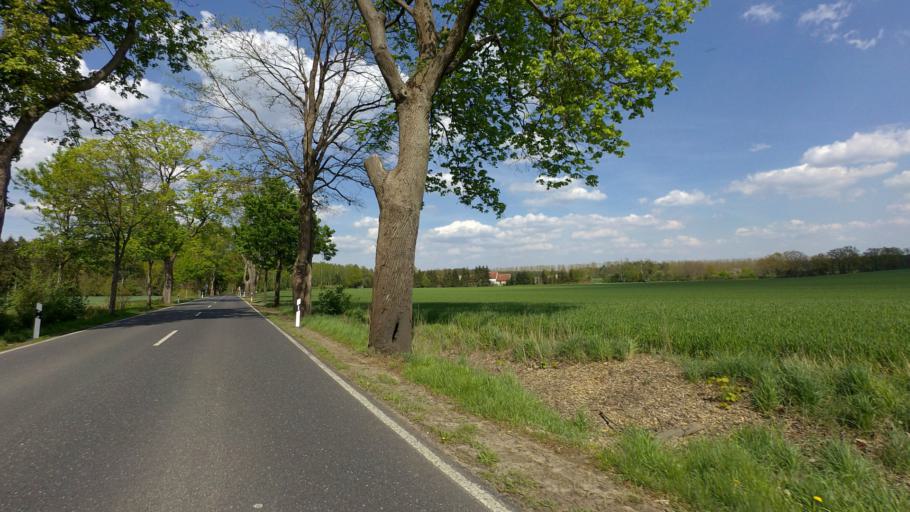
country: DE
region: Brandenburg
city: Marienwerder
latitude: 52.8838
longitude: 13.5448
